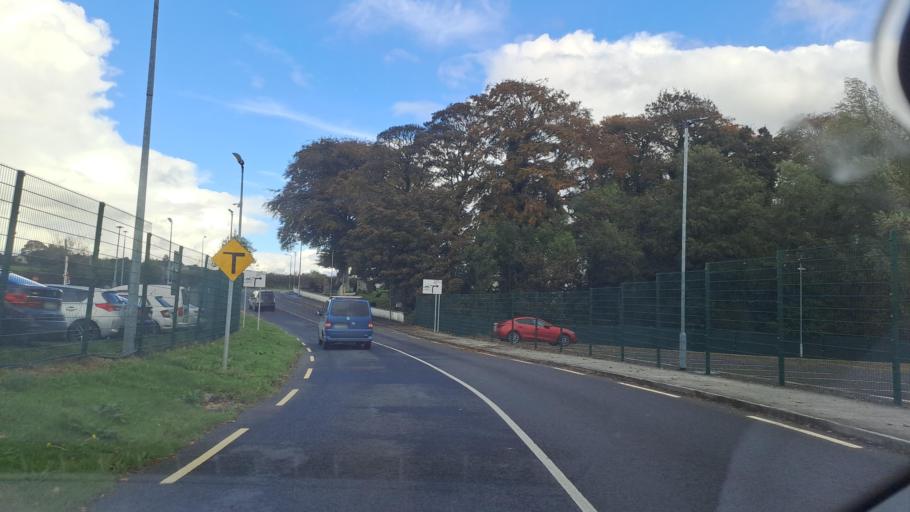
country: IE
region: Ulster
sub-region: An Cabhan
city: Bailieborough
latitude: 53.9962
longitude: -6.9030
